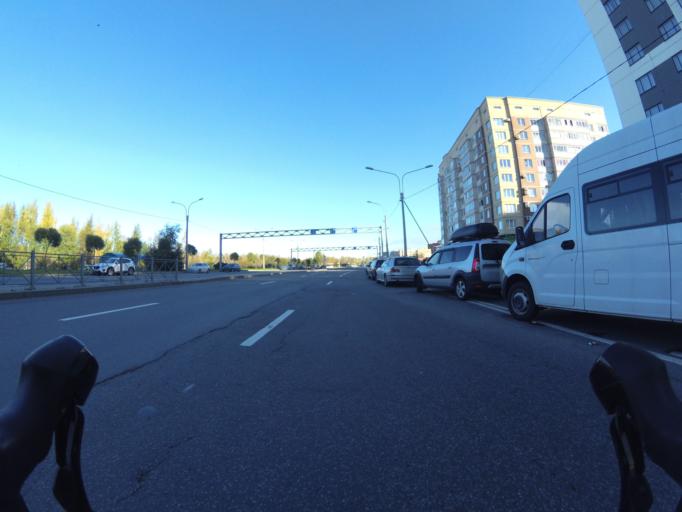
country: RU
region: Leningrad
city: Untolovo
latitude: 60.0076
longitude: 30.1998
